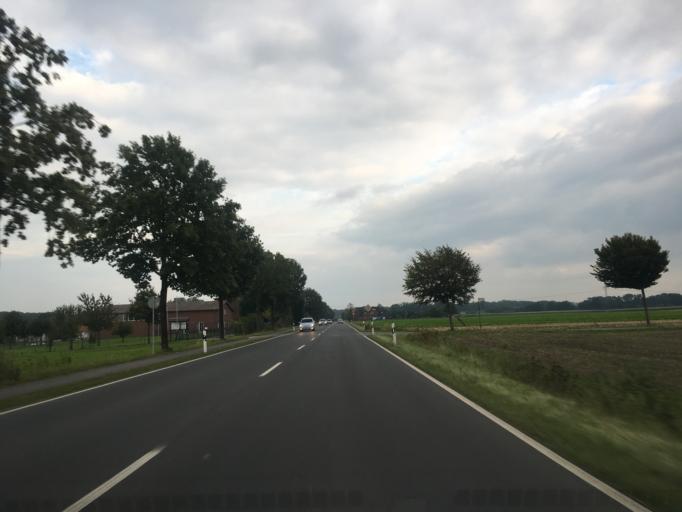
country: DE
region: North Rhine-Westphalia
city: Olfen
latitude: 51.7055
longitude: 7.3979
